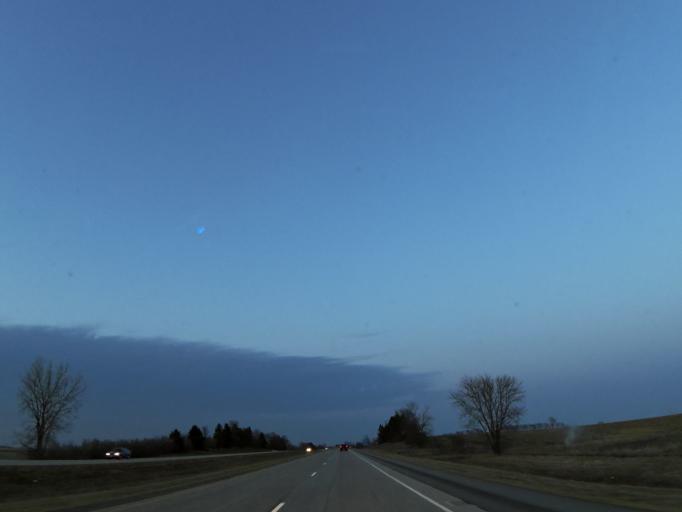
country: US
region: Minnesota
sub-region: Mower County
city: Grand Meadow
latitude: 43.7954
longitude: -92.6004
